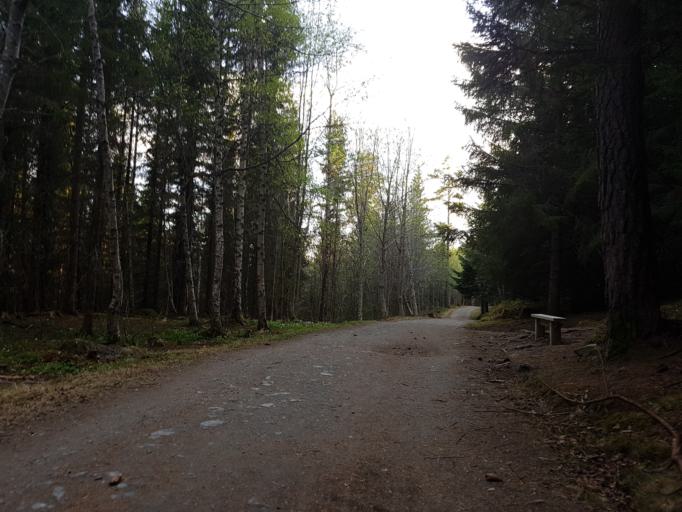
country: NO
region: Sor-Trondelag
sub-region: Trondheim
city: Trondheim
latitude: 63.4319
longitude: 10.3430
